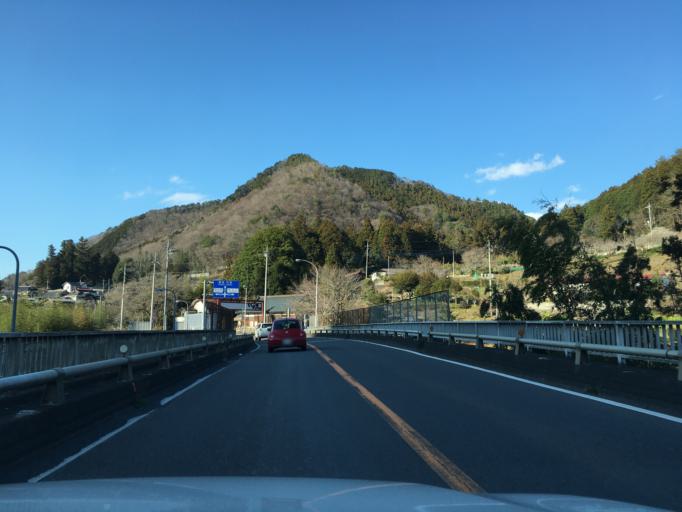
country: JP
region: Ibaraki
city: Daigo
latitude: 36.6927
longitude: 140.3892
